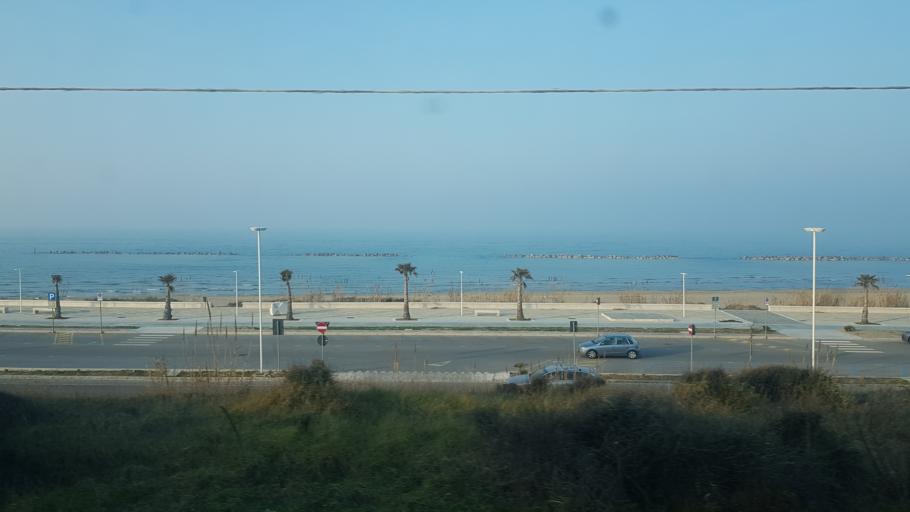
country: IT
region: Molise
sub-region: Provincia di Campobasso
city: Termoli
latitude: 42.0072
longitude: 14.9671
